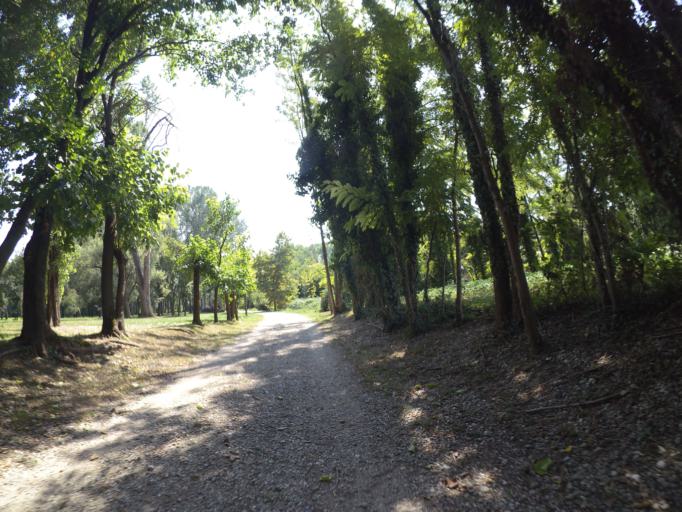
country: IT
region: Friuli Venezia Giulia
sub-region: Provincia di Udine
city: Codroipo
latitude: 45.9529
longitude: 12.9790
